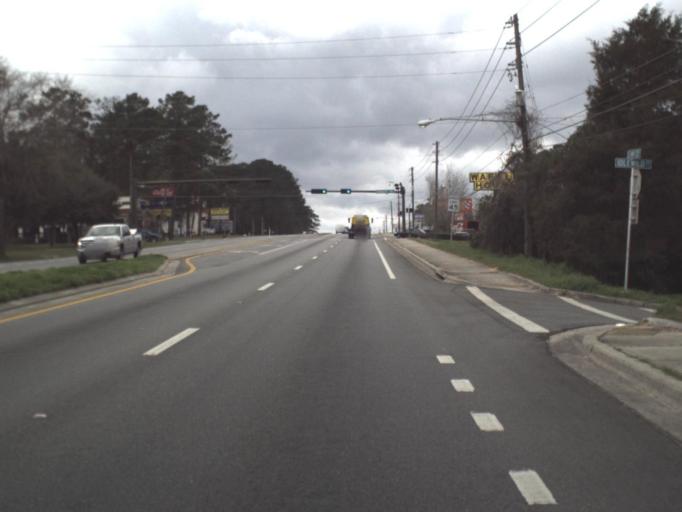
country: US
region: Florida
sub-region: Leon County
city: Tallahassee
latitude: 30.4282
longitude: -84.2151
